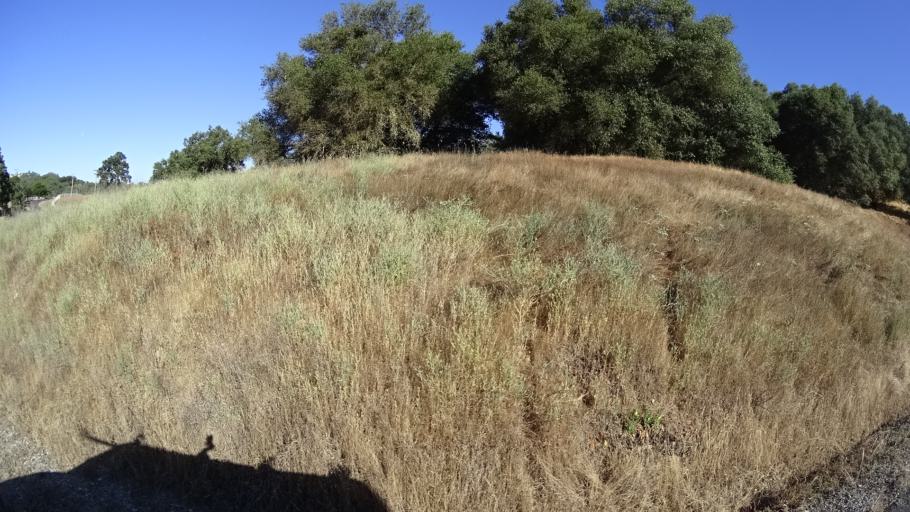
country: US
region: California
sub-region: Calaveras County
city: San Andreas
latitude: 38.2434
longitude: -120.7101
